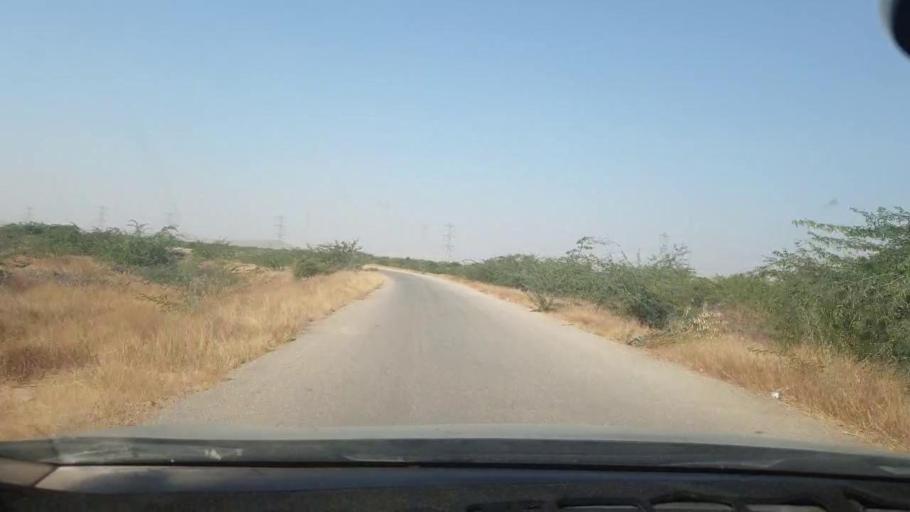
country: PK
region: Sindh
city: Malir Cantonment
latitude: 25.1626
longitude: 67.1534
